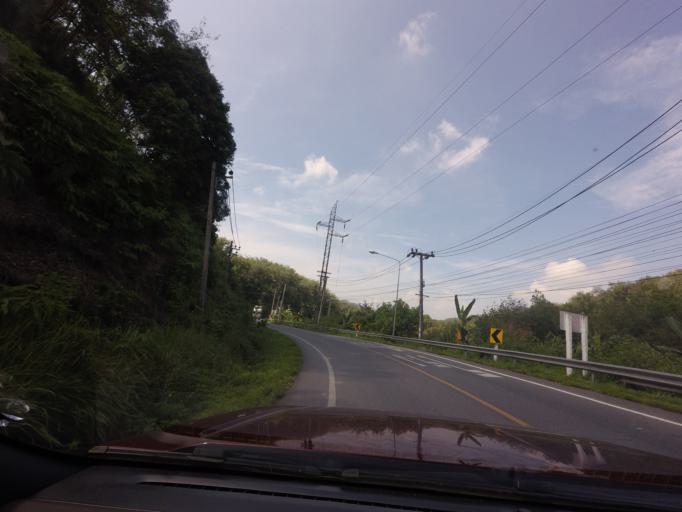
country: TH
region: Yala
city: Betong
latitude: 5.8694
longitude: 101.1283
